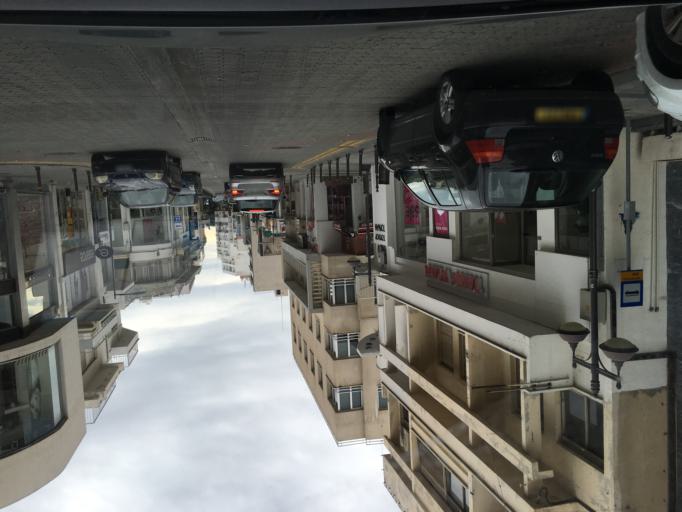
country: CY
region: Limassol
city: Limassol
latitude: 34.6786
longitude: 33.0444
